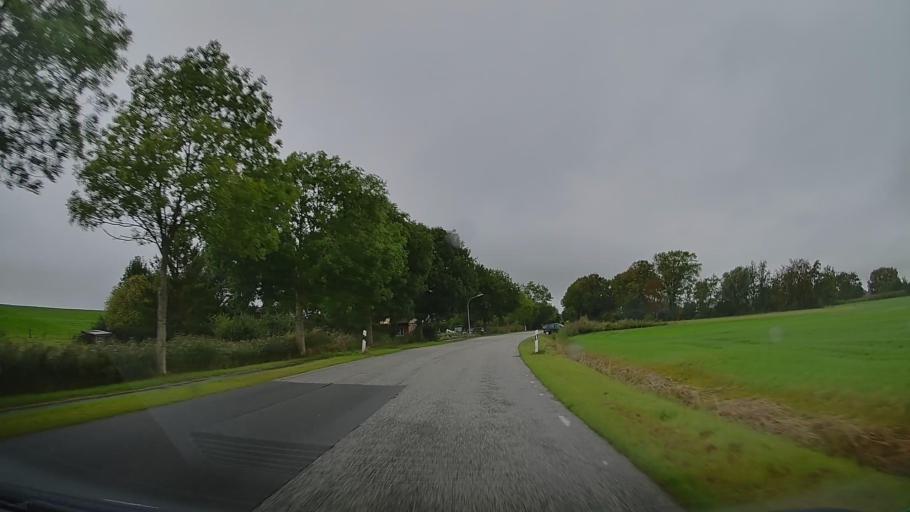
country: DE
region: Schleswig-Holstein
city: Sankt Margarethen
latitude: 53.8822
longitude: 9.2590
